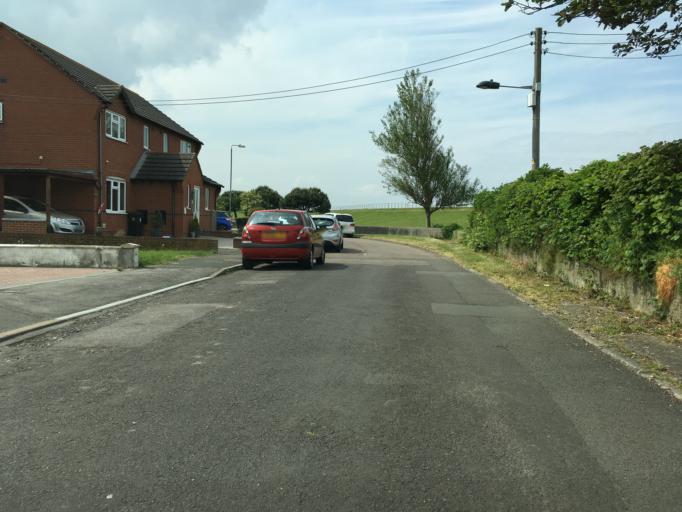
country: GB
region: England
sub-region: South Gloucestershire
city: Severn Beach
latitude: 51.5640
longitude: -2.6658
